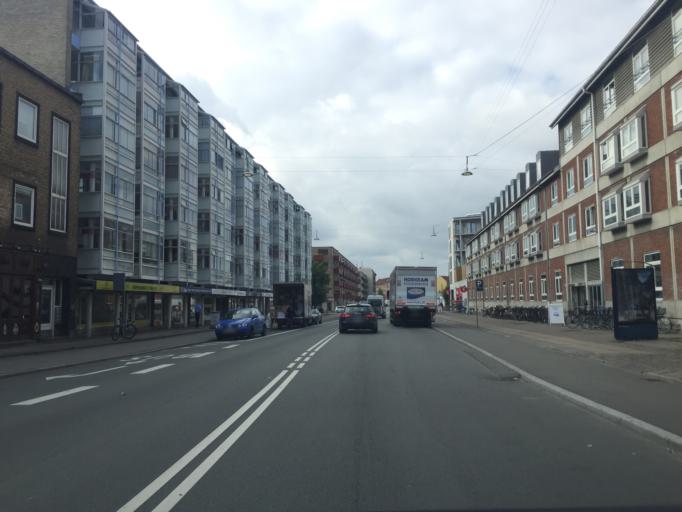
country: DK
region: Capital Region
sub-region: Frederiksberg Kommune
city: Frederiksberg
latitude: 55.7085
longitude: 12.5321
